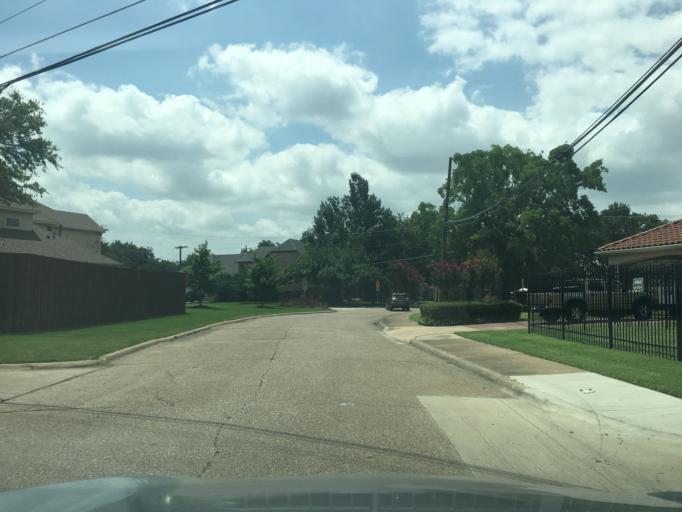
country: US
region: Texas
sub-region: Dallas County
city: Addison
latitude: 32.9149
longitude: -96.8236
